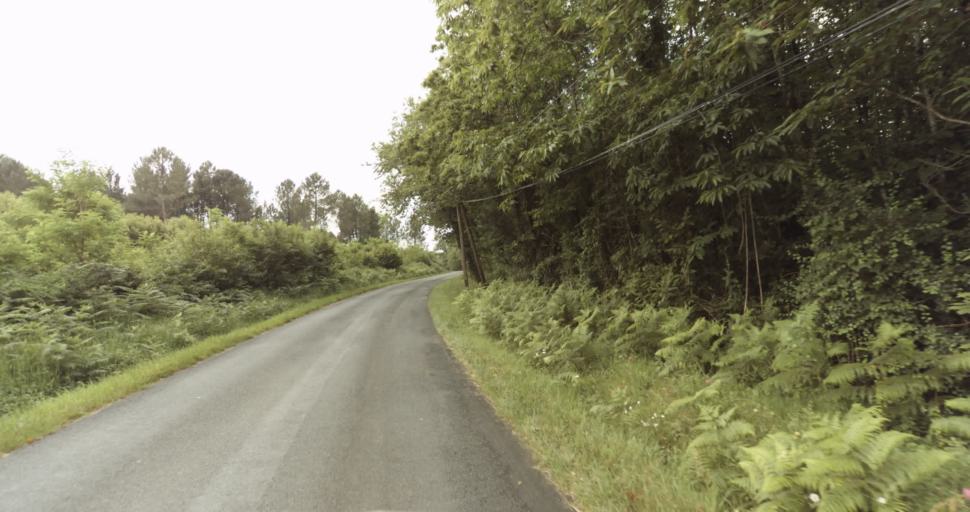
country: FR
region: Aquitaine
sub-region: Departement de la Dordogne
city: Le Bugue
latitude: 44.9388
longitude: 0.8198
